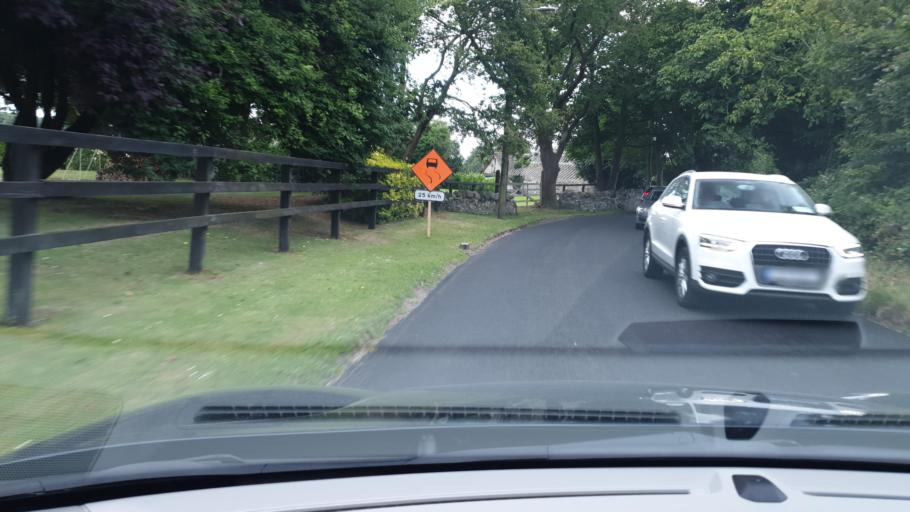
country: IE
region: Leinster
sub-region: Fingal County
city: Skerries
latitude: 53.5827
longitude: -6.1475
